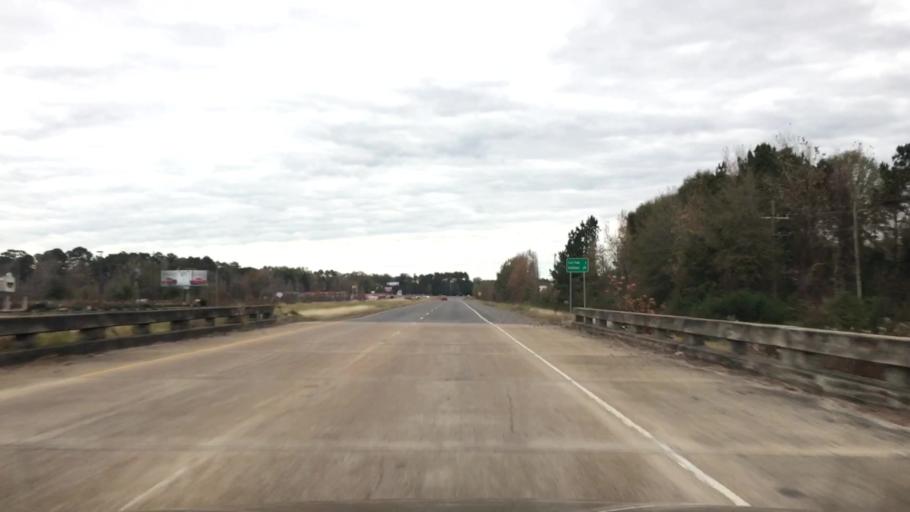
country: US
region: Louisiana
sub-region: Vernon Parish
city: New Llano
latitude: 31.1076
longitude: -93.2709
